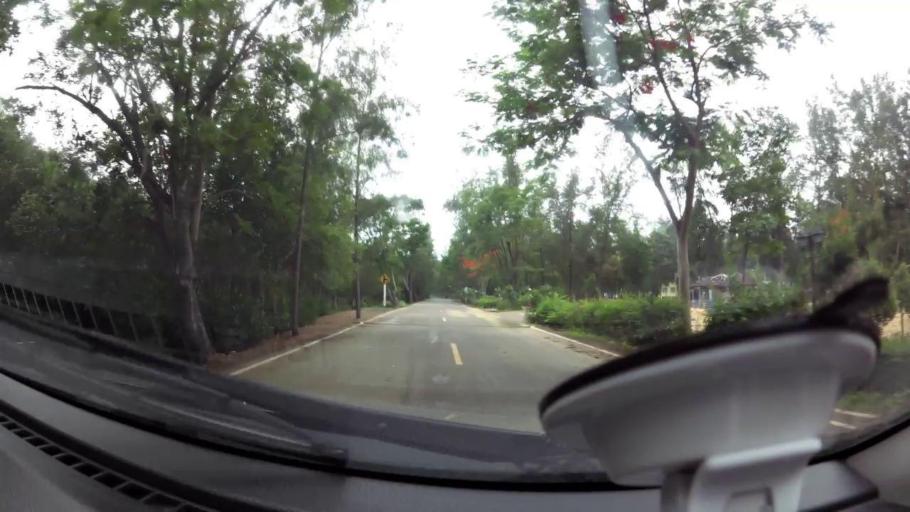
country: TH
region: Prachuap Khiri Khan
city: Pran Buri
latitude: 12.4138
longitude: 99.9851
